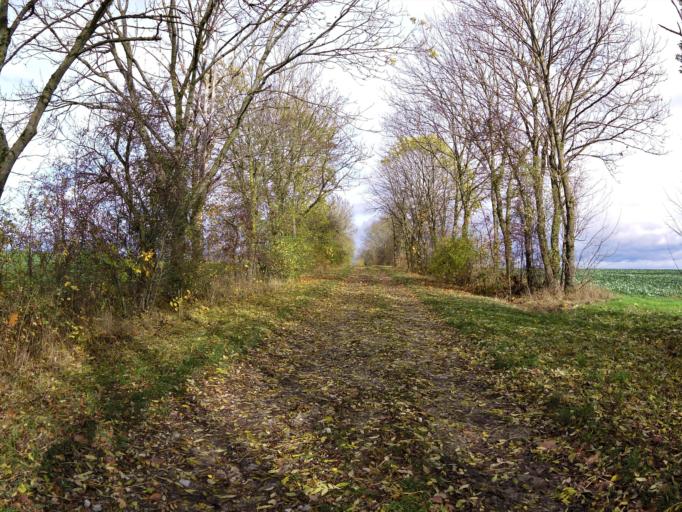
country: DE
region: Hesse
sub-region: Regierungsbezirk Kassel
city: Herleshausen
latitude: 51.0548
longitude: 10.1281
